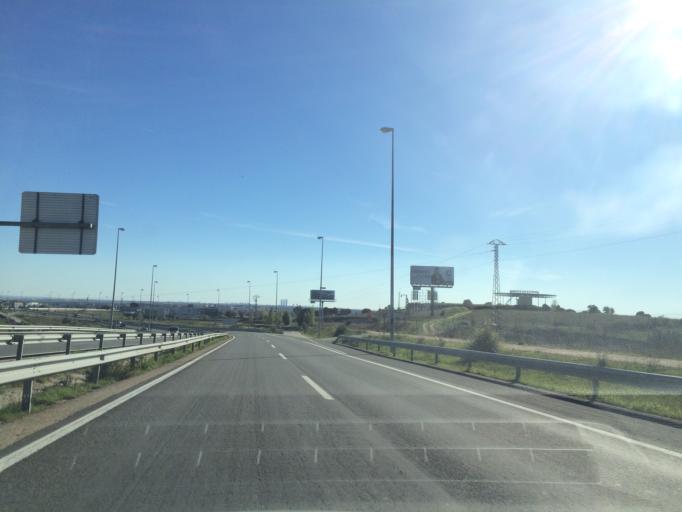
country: ES
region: Madrid
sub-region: Provincia de Madrid
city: Colmenar Viejo
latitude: 40.6490
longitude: -3.7352
